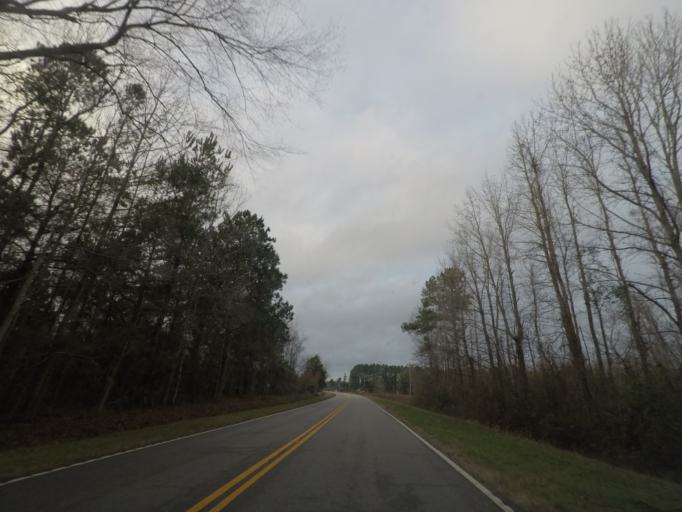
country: US
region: South Carolina
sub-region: Dorchester County
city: Saint George
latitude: 33.0743
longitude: -80.6371
